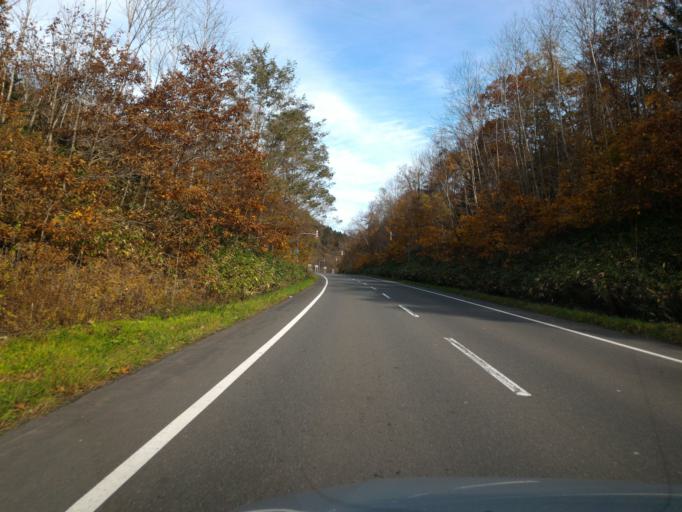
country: JP
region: Hokkaido
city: Shimo-furano
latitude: 43.3582
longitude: 142.3037
